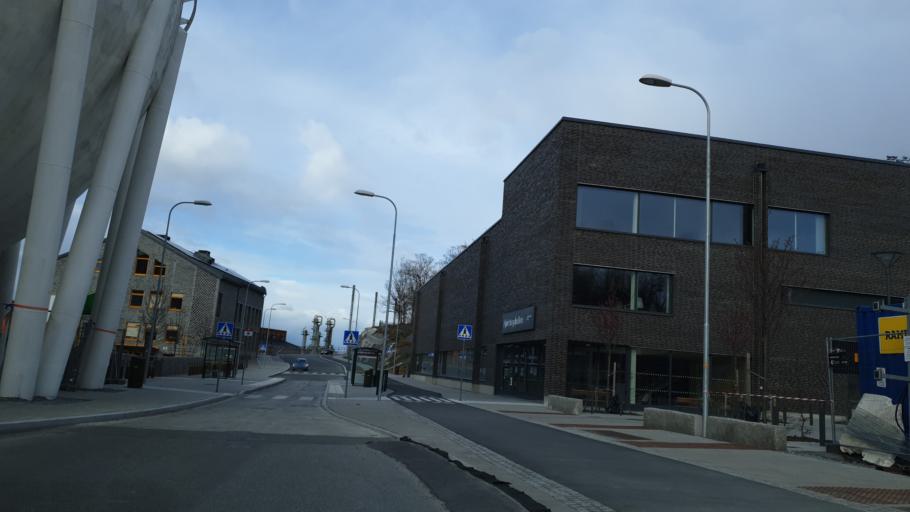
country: SE
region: Stockholm
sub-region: Stockholms Kommun
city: OEstermalm
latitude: 59.3568
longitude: 18.0921
